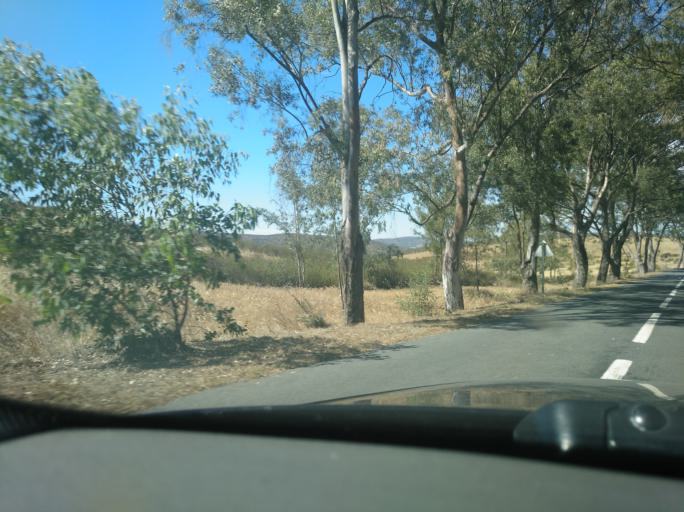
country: PT
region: Beja
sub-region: Mertola
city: Mertola
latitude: 37.6173
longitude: -7.7771
